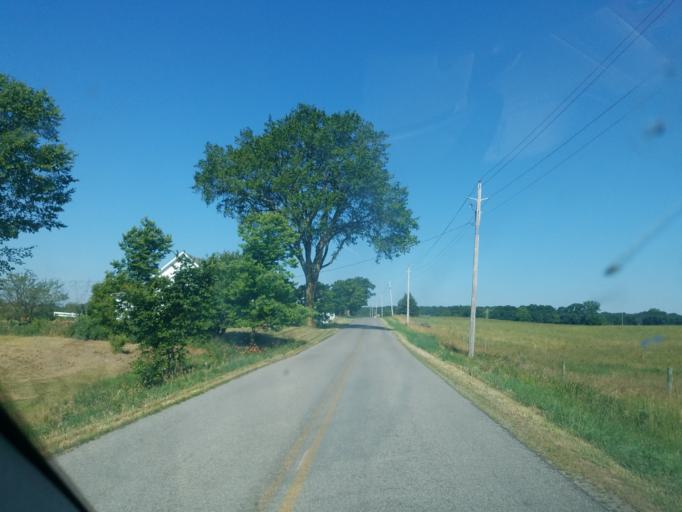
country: US
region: Ohio
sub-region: Logan County
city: Northwood
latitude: 40.4415
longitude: -83.6829
